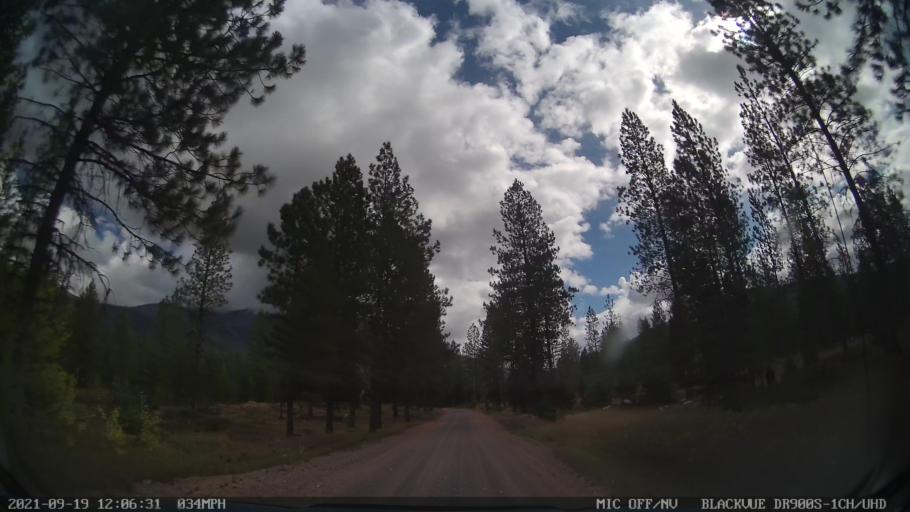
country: US
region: Montana
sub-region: Missoula County
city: Seeley Lake
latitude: 47.1850
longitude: -113.4182
